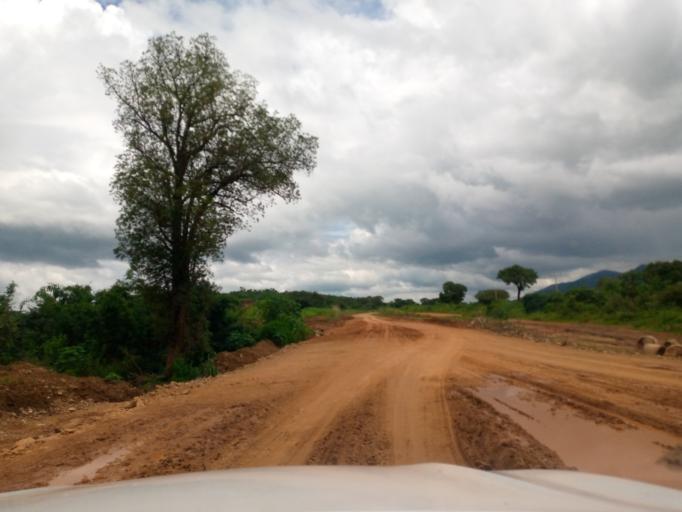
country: ET
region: Oromiya
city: Mendi
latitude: 10.1962
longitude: 35.0919
